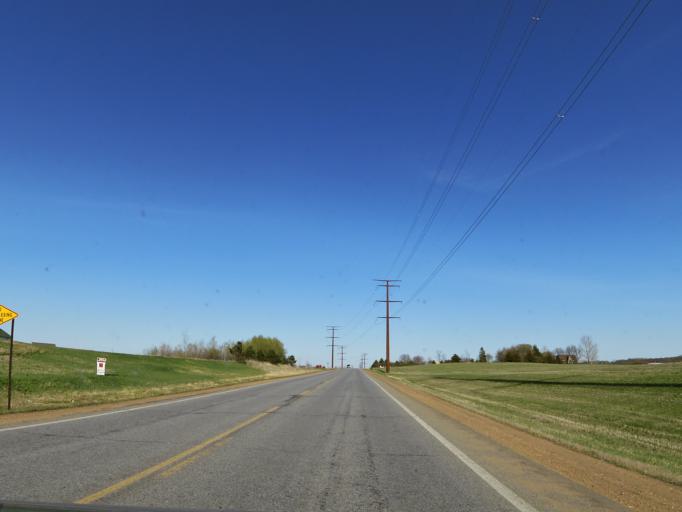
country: US
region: Minnesota
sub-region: Le Sueur County
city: New Prague
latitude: 44.5726
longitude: -93.4955
